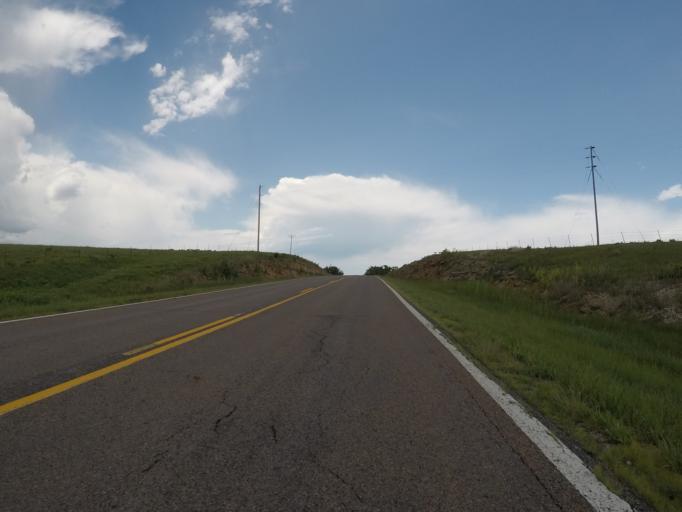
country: US
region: Kansas
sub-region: Wabaunsee County
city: Alma
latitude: 38.8692
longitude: -96.3301
